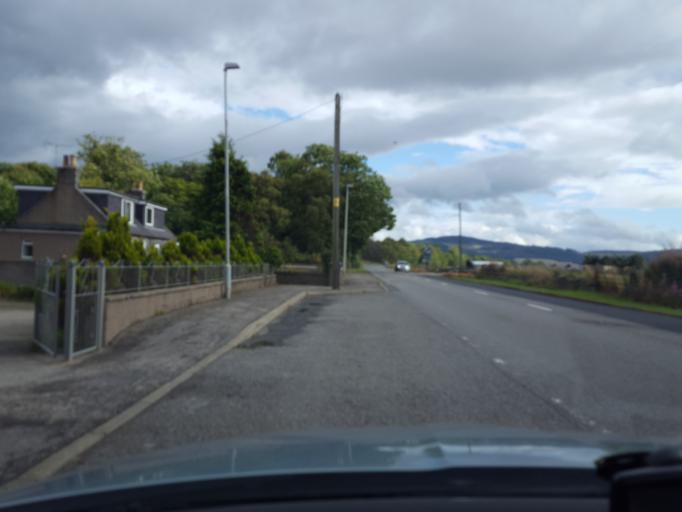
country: GB
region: Scotland
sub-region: Aberdeenshire
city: Alford
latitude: 57.2319
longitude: -2.6842
